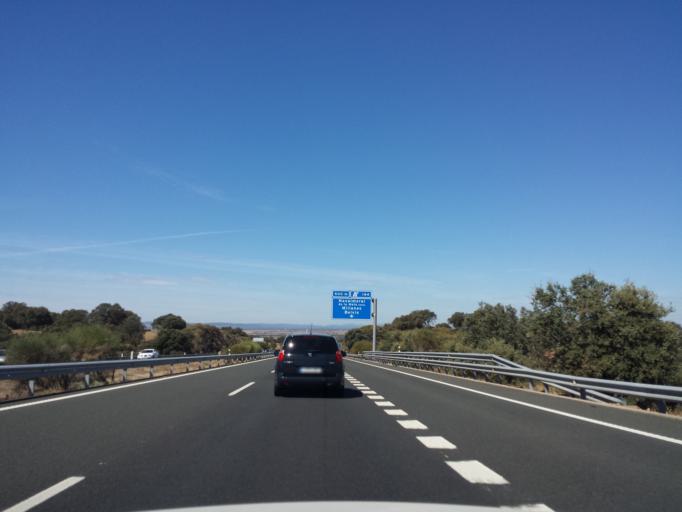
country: ES
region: Extremadura
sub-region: Provincia de Caceres
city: Millanes
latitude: 39.8729
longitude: -5.5637
